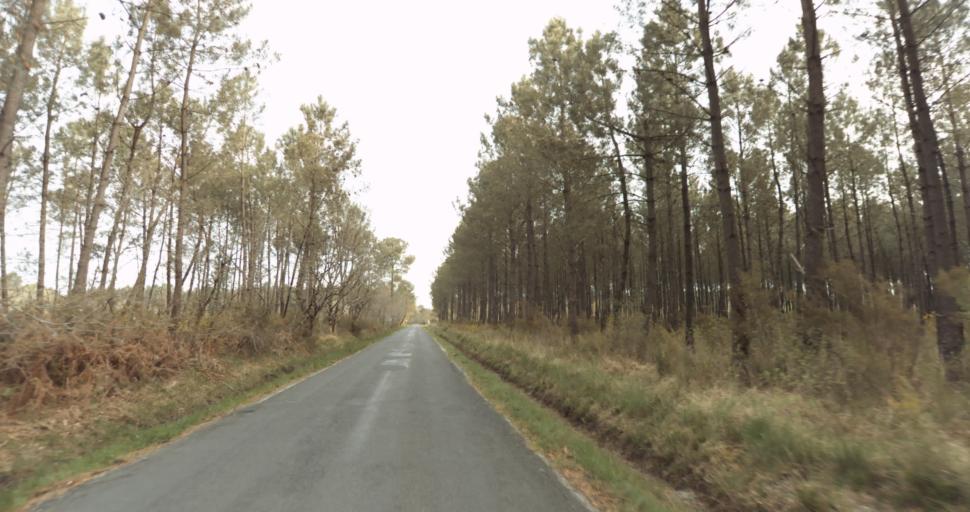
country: FR
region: Aquitaine
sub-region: Departement de la Gironde
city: Martignas-sur-Jalle
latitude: 44.8001
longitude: -0.7663
